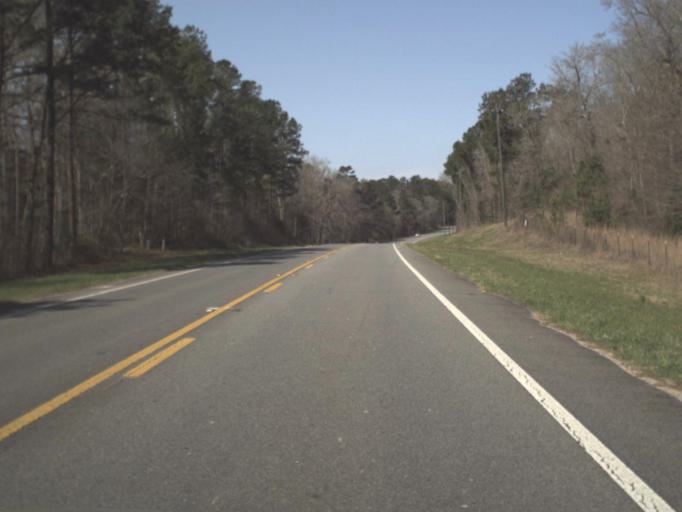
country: US
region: Florida
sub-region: Gadsden County
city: Quincy
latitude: 30.5932
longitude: -84.5250
